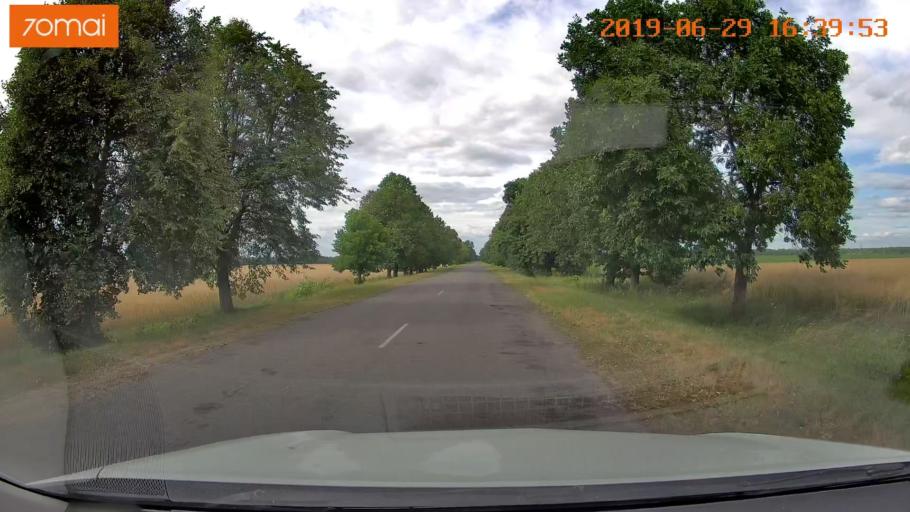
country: BY
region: Brest
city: Luninyets
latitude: 52.2482
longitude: 27.0167
